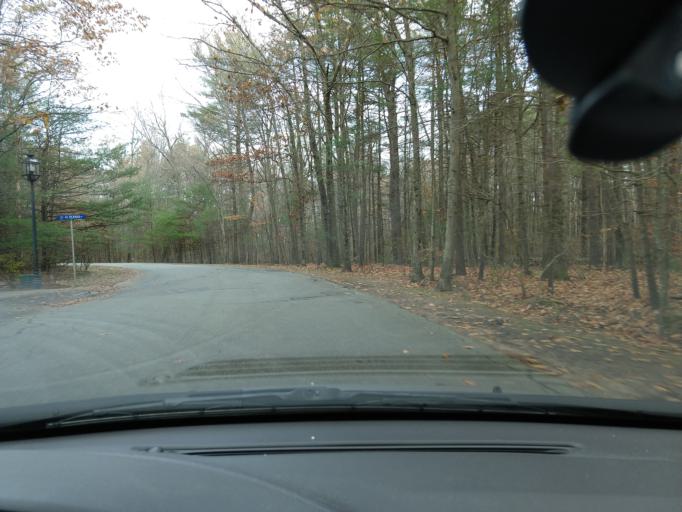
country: US
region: Massachusetts
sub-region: Middlesex County
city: Bedford
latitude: 42.5088
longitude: -71.2884
